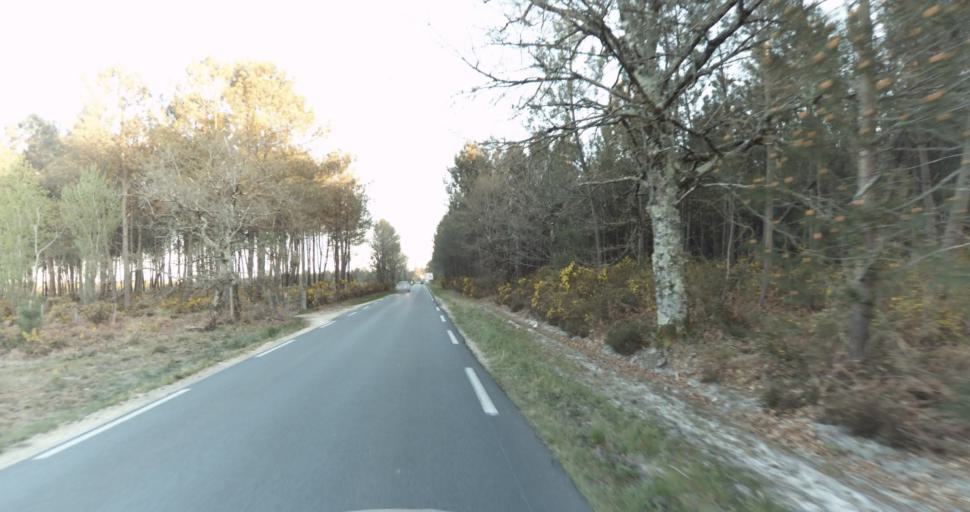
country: FR
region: Aquitaine
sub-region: Departement de la Gironde
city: Martignas-sur-Jalle
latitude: 44.8290
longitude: -0.7647
